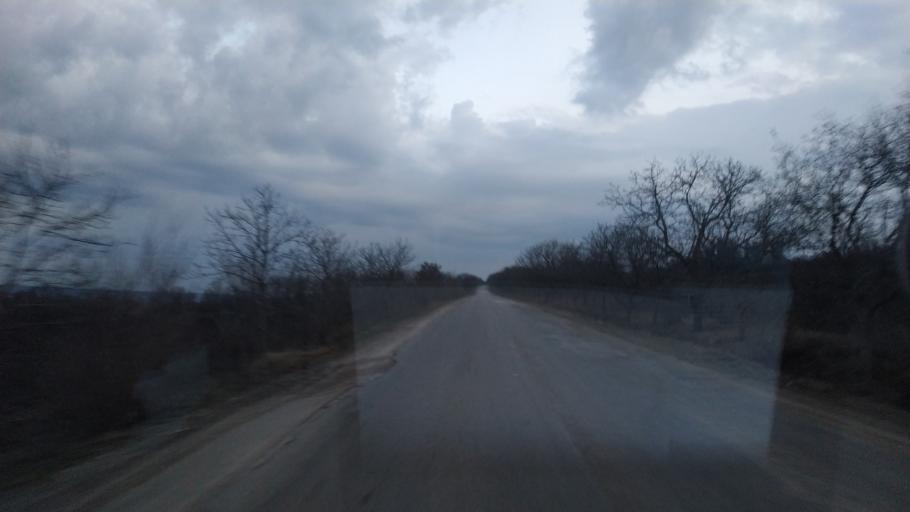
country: MD
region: Anenii Noi
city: Anenii Noi
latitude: 46.9416
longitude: 29.2843
